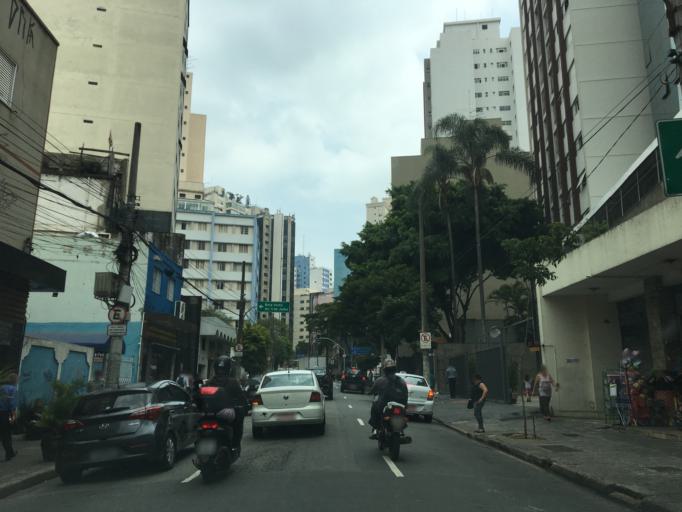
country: BR
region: Sao Paulo
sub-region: Sao Paulo
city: Sao Paulo
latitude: -23.5563
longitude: -46.6556
